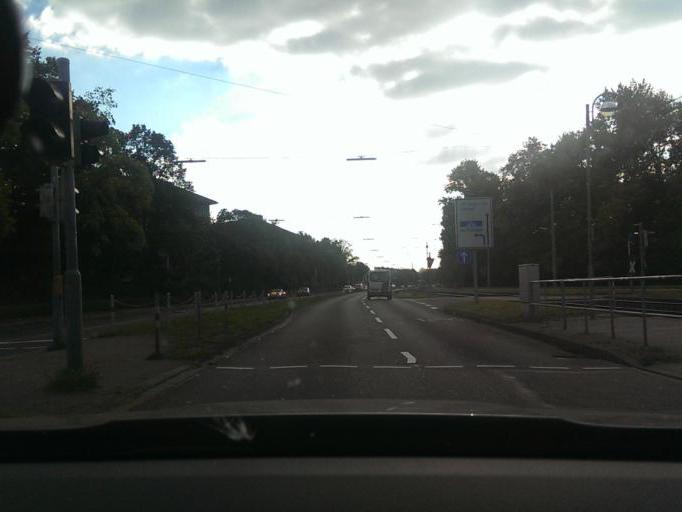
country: DE
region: Baden-Wuerttemberg
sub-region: Karlsruhe Region
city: Karlsruhe
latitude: 49.0171
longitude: 8.4389
